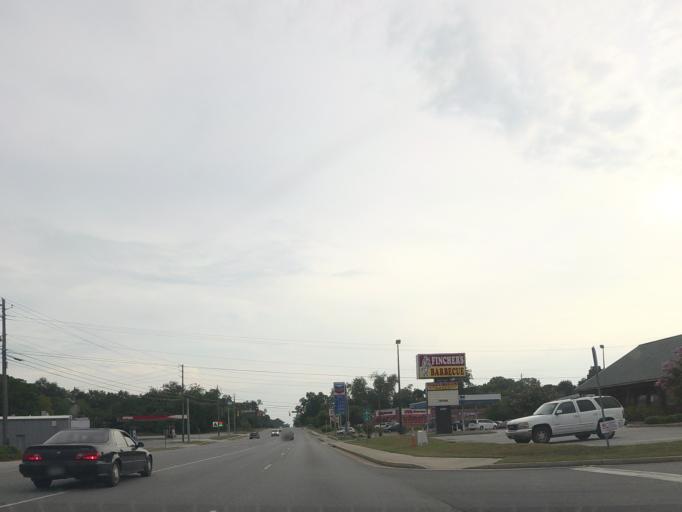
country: US
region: Georgia
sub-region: Bibb County
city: Macon
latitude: 32.7472
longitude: -83.6719
